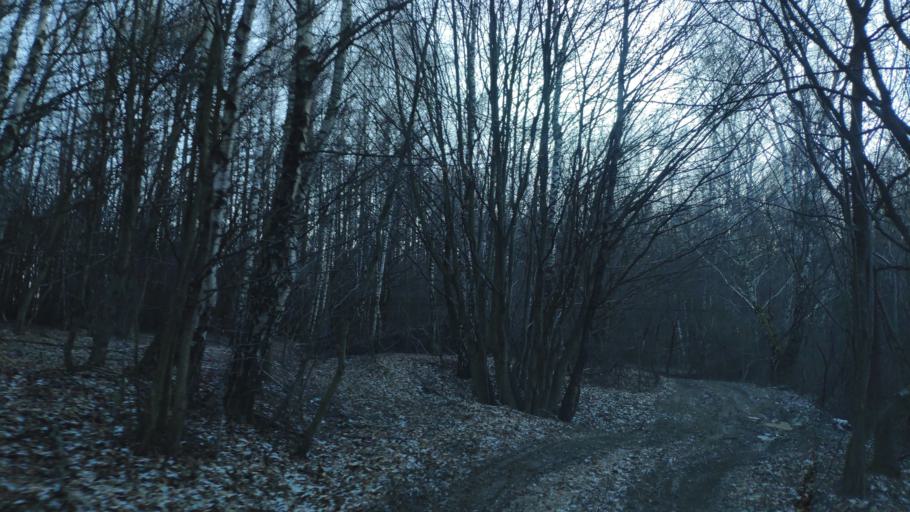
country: SK
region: Kosicky
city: Kosice
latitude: 48.8524
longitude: 21.2377
